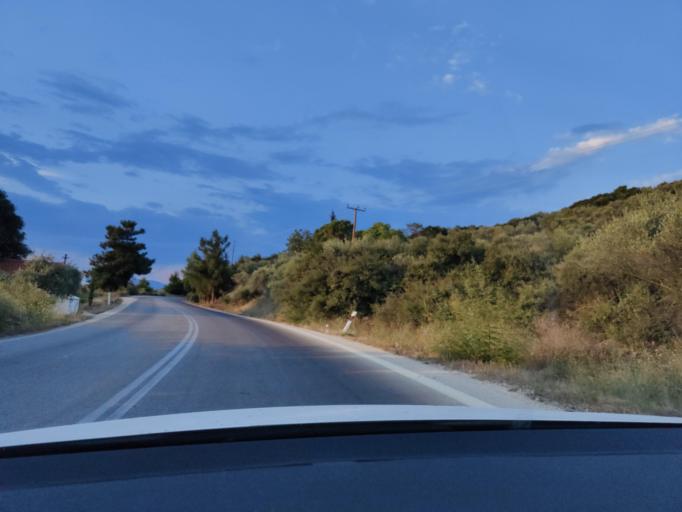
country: GR
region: East Macedonia and Thrace
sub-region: Nomos Kavalas
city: Prinos
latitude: 40.7647
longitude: 24.5970
